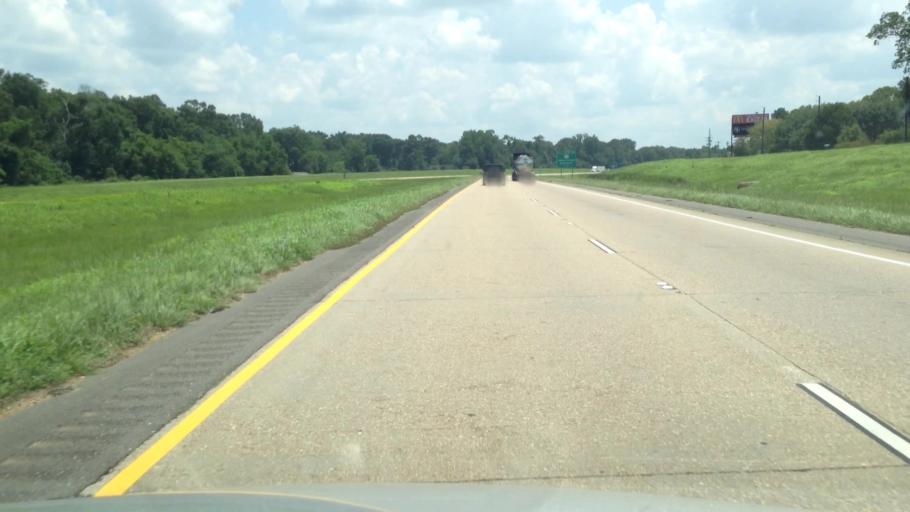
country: US
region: Louisiana
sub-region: Saint Landry Parish
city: Opelousas
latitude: 30.5512
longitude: -92.0530
